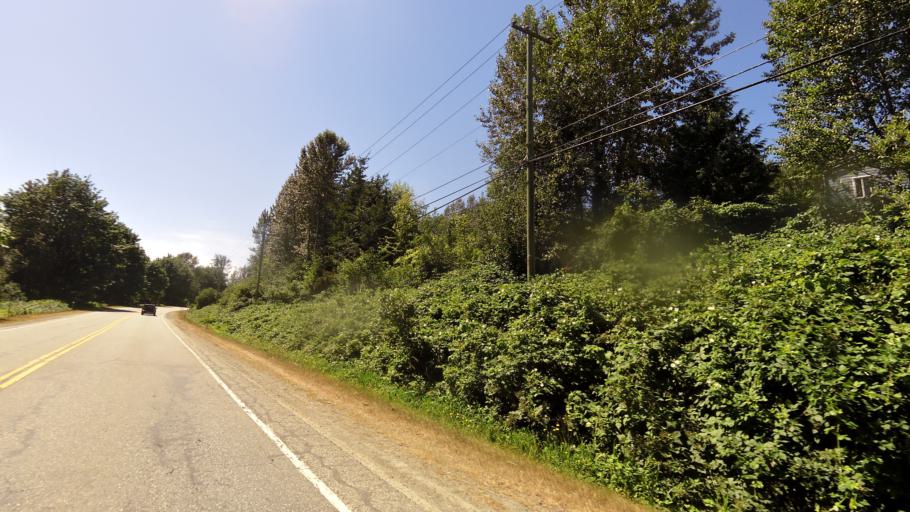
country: CA
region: British Columbia
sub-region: Fraser Valley Regional District
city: Chilliwack
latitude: 49.2044
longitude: -122.0263
